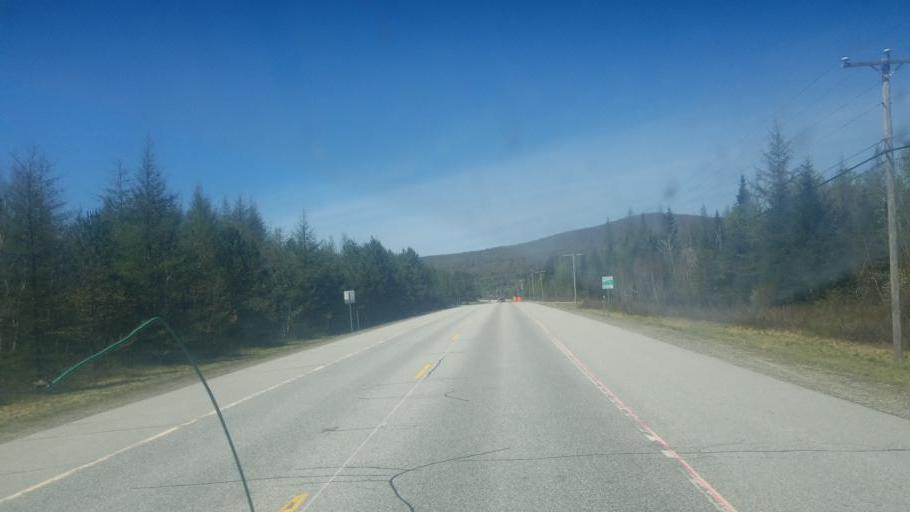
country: US
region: New Hampshire
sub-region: Coos County
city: Jefferson
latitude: 44.2658
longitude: -71.4630
